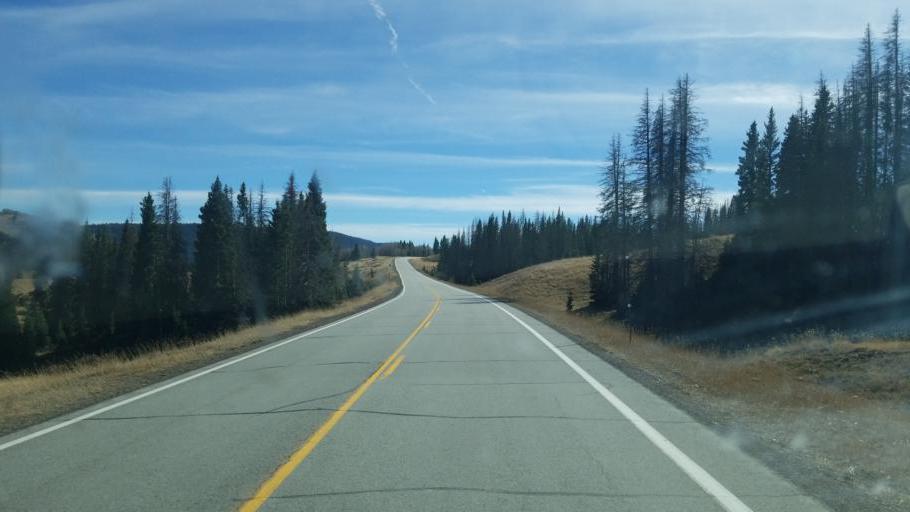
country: US
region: New Mexico
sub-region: Rio Arriba County
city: Chama
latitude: 37.0330
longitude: -106.4130
